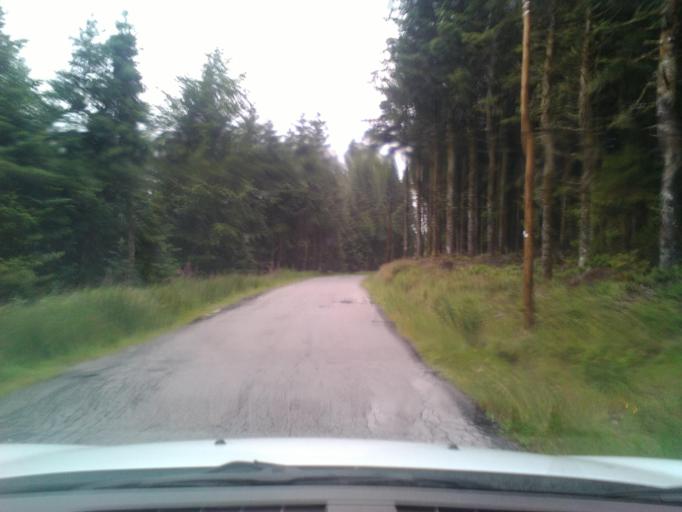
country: FR
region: Lorraine
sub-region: Departement des Vosges
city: Gerardmer
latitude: 48.0899
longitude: 6.8491
